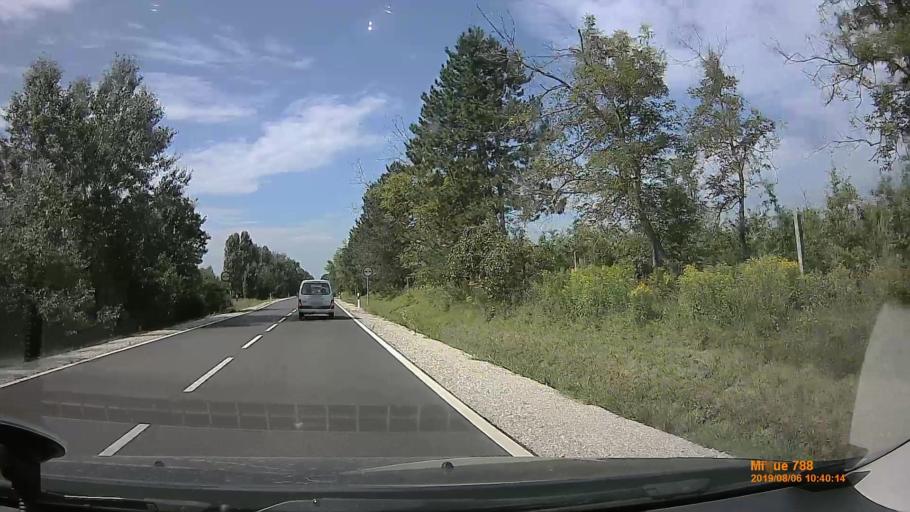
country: HU
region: Zala
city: Zalakomar
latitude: 46.5263
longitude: 17.1549
